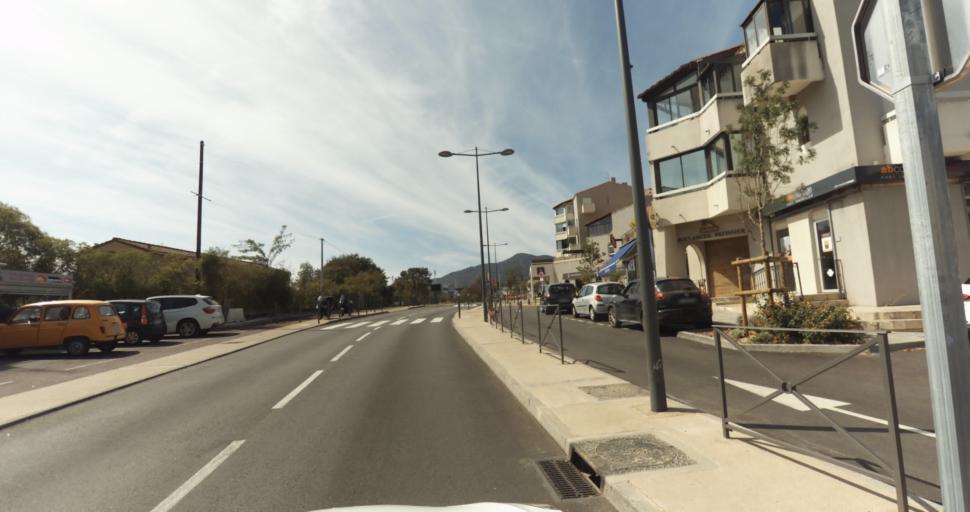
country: FR
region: Corsica
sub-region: Departement de la Corse-du-Sud
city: Afa
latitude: 41.9520
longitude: 8.7781
